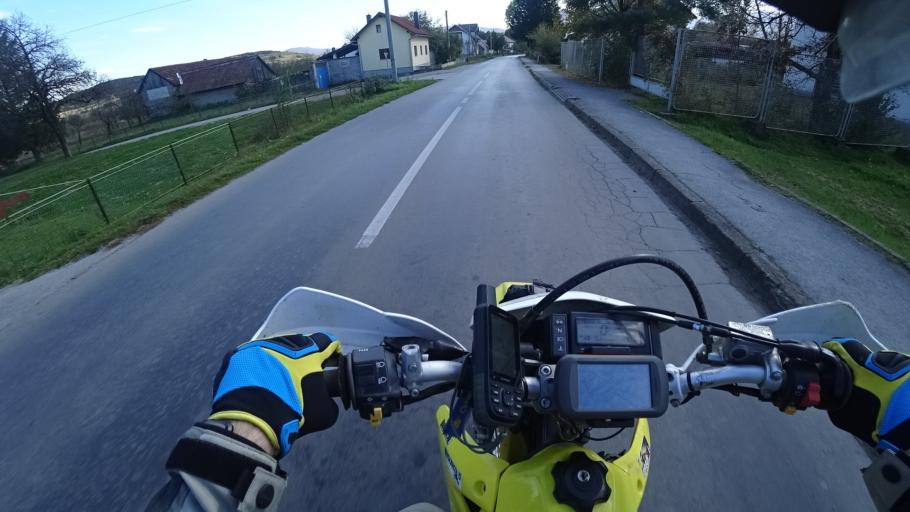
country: HR
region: Karlovacka
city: Plaski
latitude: 45.0884
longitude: 15.3651
